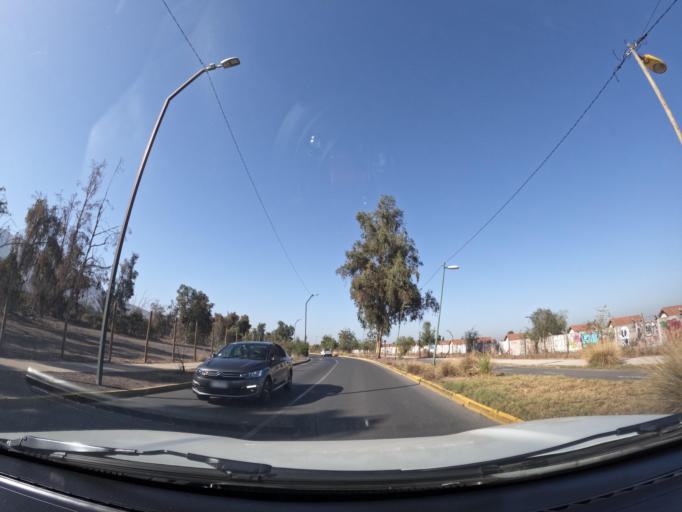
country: CL
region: Santiago Metropolitan
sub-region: Provincia de Santiago
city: Villa Presidente Frei, Nunoa, Santiago, Chile
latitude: -33.5035
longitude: -70.5438
